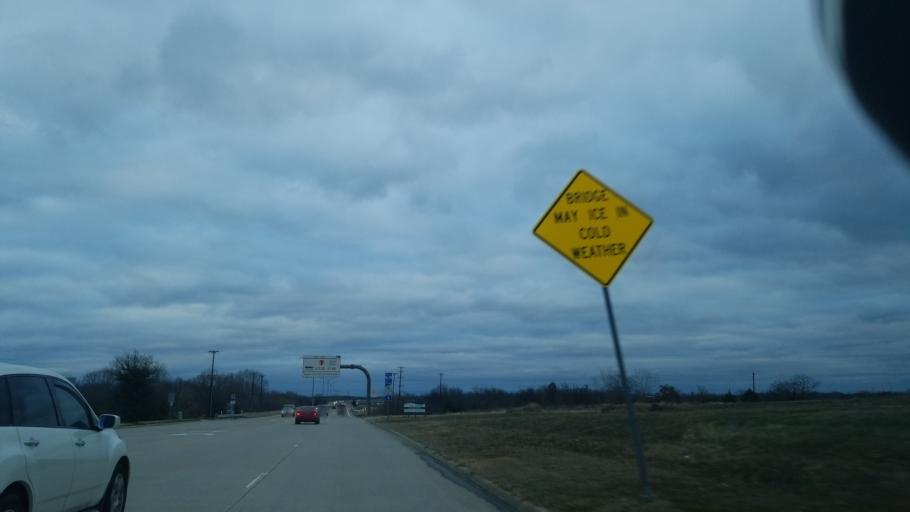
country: US
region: Texas
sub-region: Denton County
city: Lake Dallas
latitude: 33.1333
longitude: -97.0235
